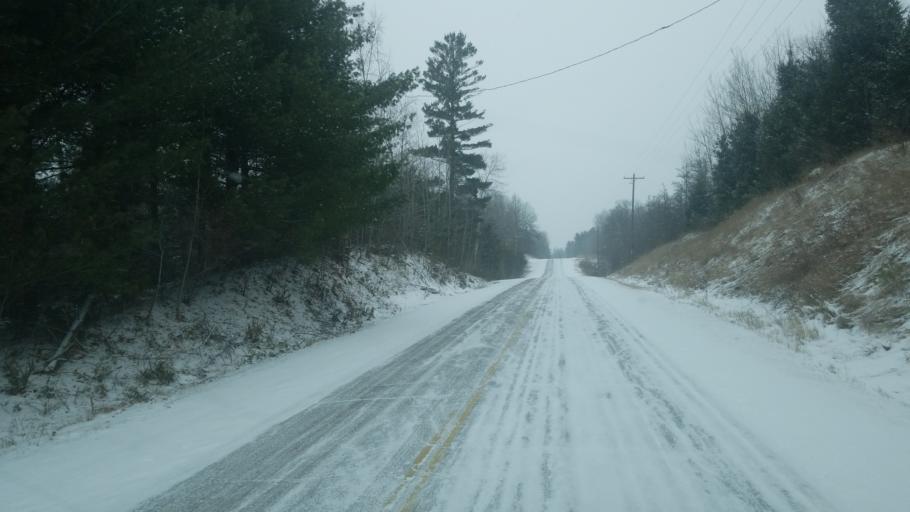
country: US
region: Michigan
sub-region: Osceola County
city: Reed City
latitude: 43.8012
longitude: -85.4025
